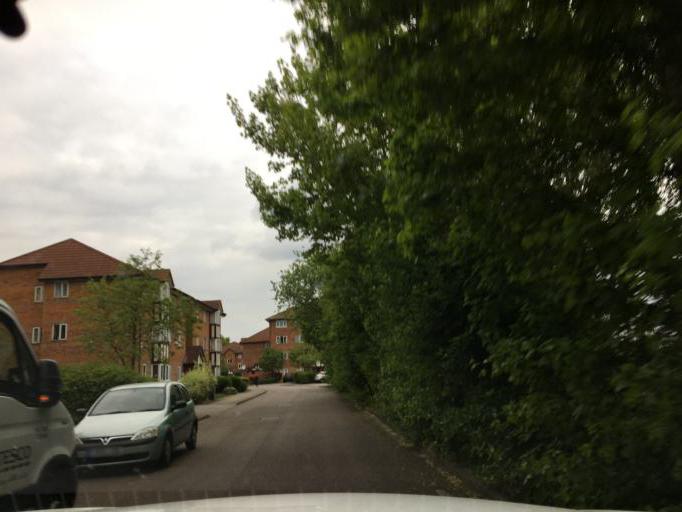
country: GB
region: England
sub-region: Greater London
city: Blackheath
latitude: 51.4395
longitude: 0.0102
